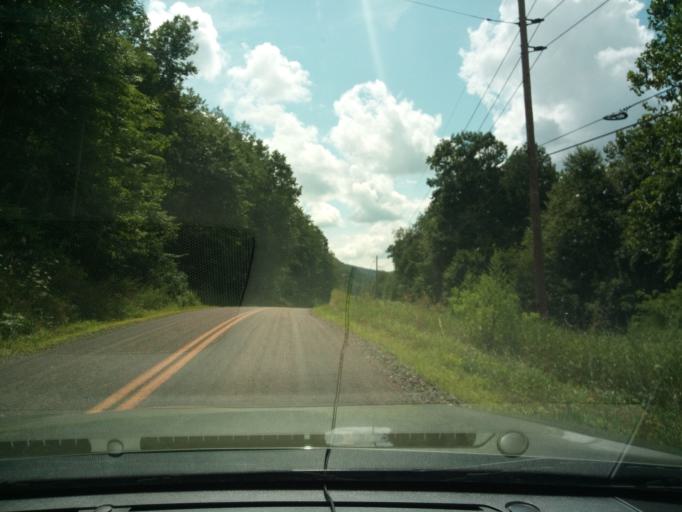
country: US
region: Pennsylvania
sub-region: Bradford County
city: South Waverly
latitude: 41.9944
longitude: -76.5986
